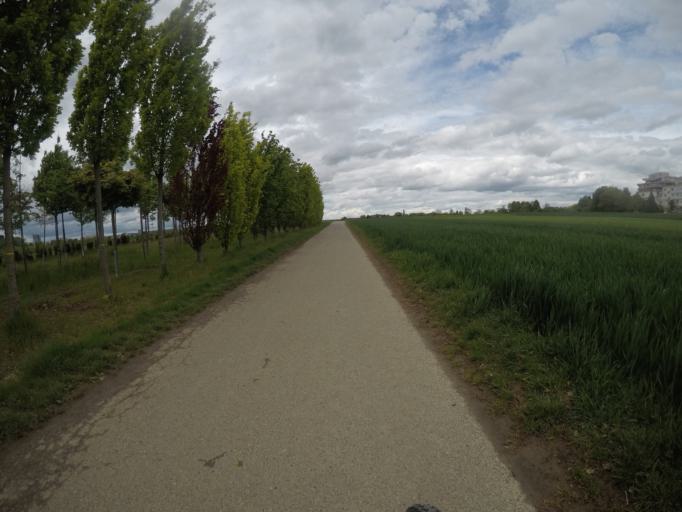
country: DE
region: Baden-Wuerttemberg
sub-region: Regierungsbezirk Stuttgart
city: Leinfelden-Echterdingen
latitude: 48.7318
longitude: 9.1345
